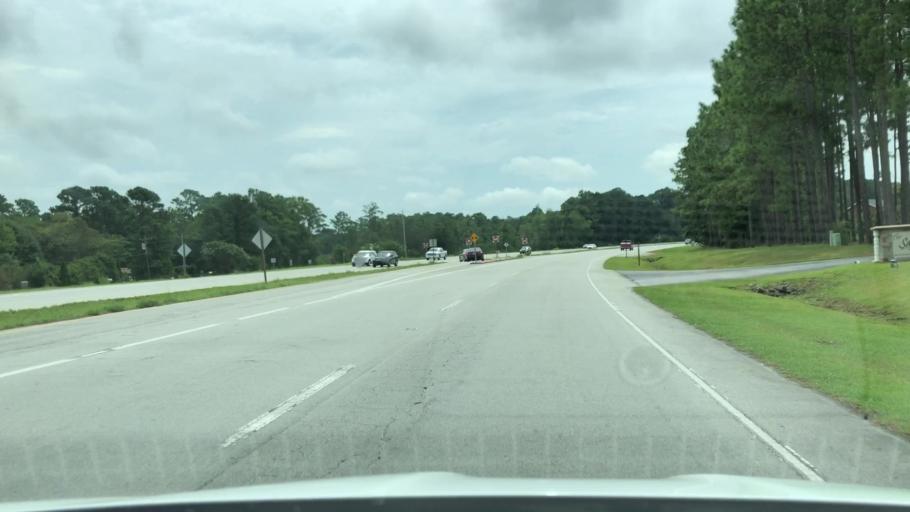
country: US
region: North Carolina
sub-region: Carteret County
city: Newport
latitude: 34.8264
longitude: -76.8765
